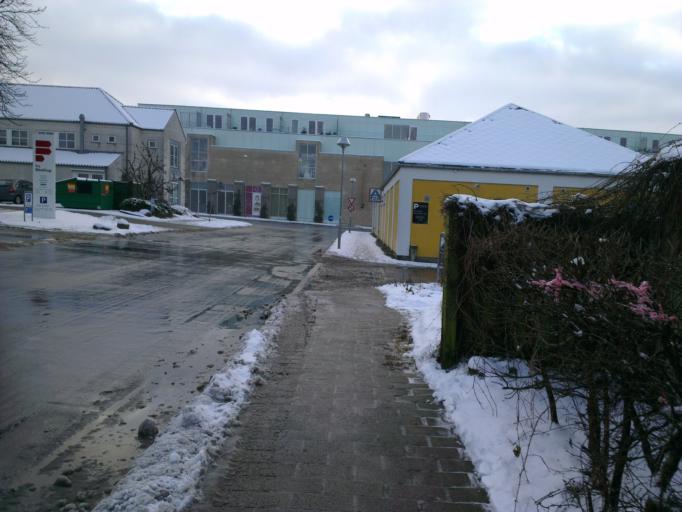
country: DK
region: Capital Region
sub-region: Frederikssund Kommune
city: Frederikssund
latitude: 55.8371
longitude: 12.0639
